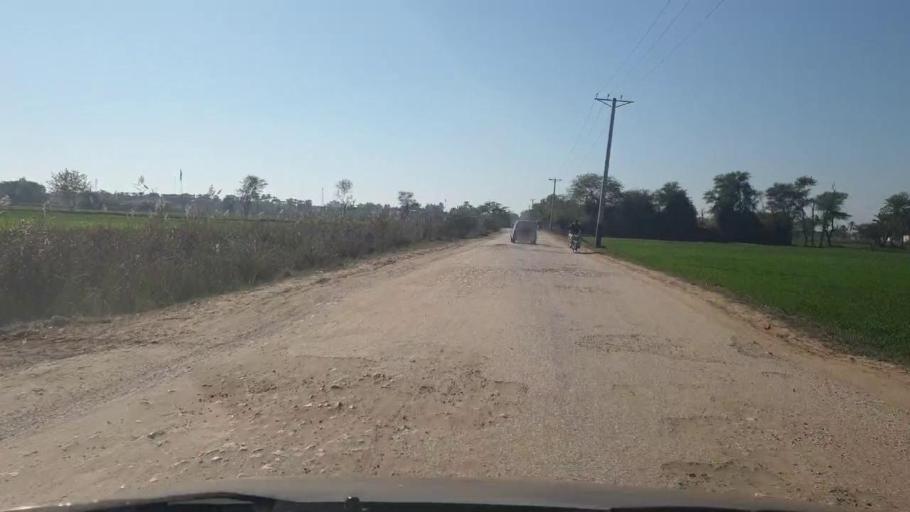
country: PK
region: Sindh
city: Bozdar
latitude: 27.0780
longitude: 68.6174
